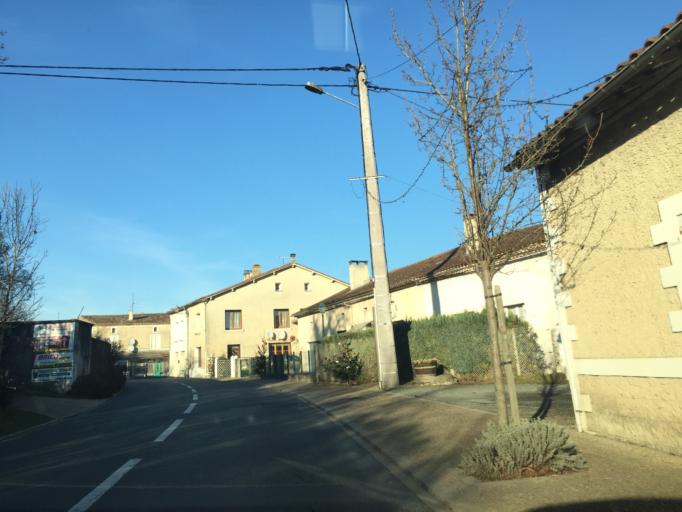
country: FR
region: Aquitaine
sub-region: Departement de la Dordogne
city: Neuvic
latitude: 45.1620
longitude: 0.3979
